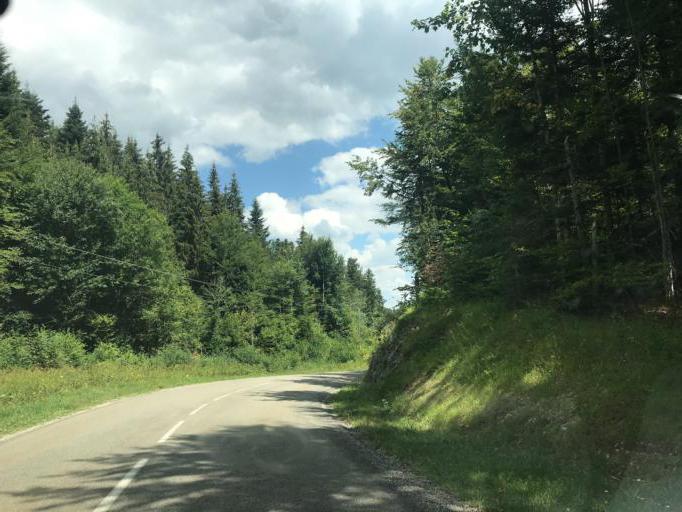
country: FR
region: Franche-Comte
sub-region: Departement du Jura
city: Clairvaux-les-Lacs
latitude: 46.5235
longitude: 5.7953
